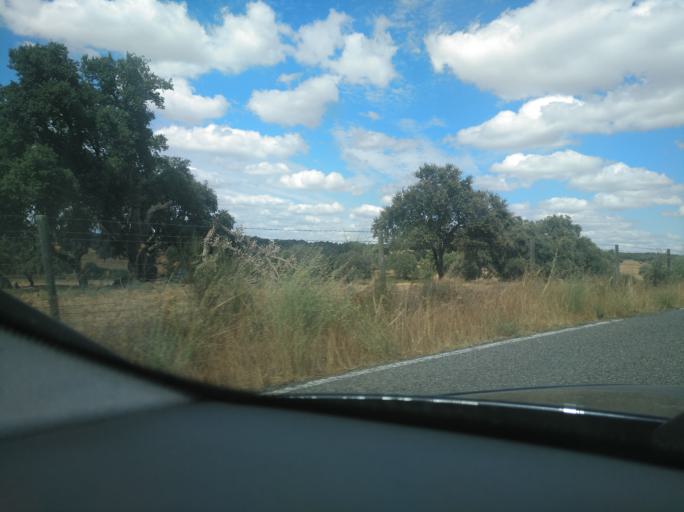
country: PT
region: Portalegre
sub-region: Arronches
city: Arronches
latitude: 39.0715
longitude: -7.3943
